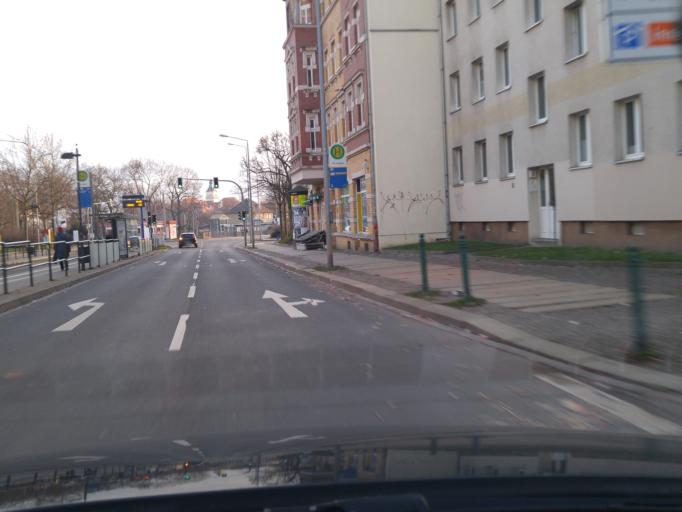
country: DE
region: Saxony
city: Leipzig
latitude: 51.3682
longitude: 12.3662
